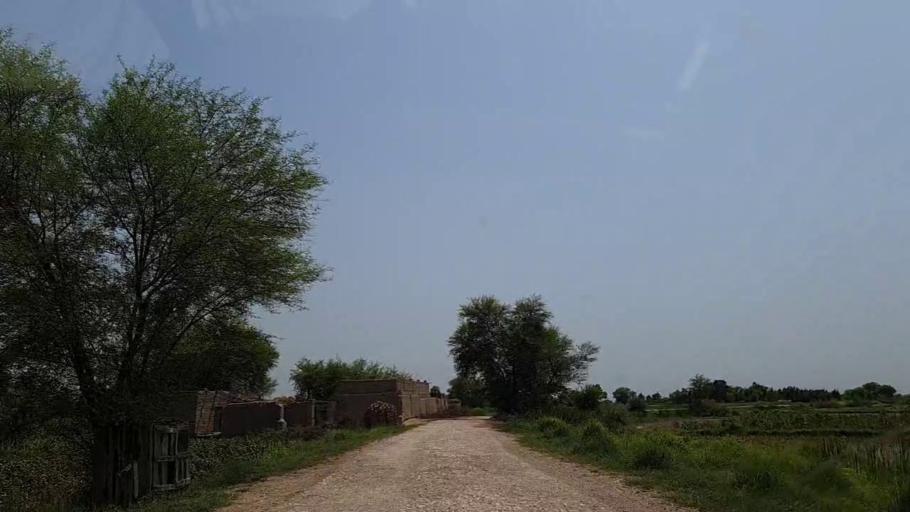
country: PK
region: Sindh
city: Ghotki
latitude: 27.9806
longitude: 69.4031
